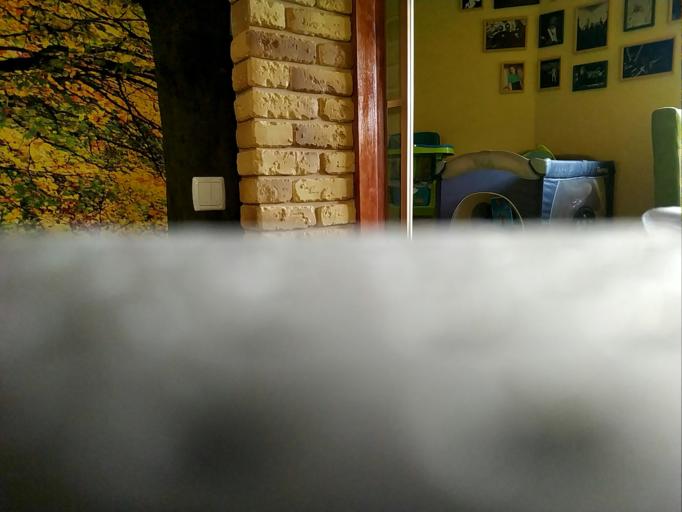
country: RU
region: Kaluga
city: Seredeyskiy
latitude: 53.9850
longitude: 35.3232
